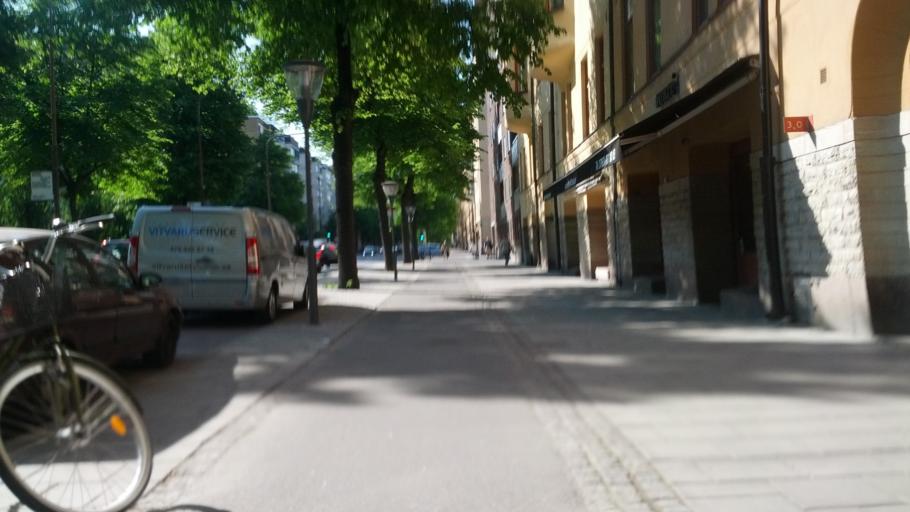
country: SE
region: Stockholm
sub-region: Stockholms Kommun
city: Stockholm
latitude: 59.3504
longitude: 18.0578
